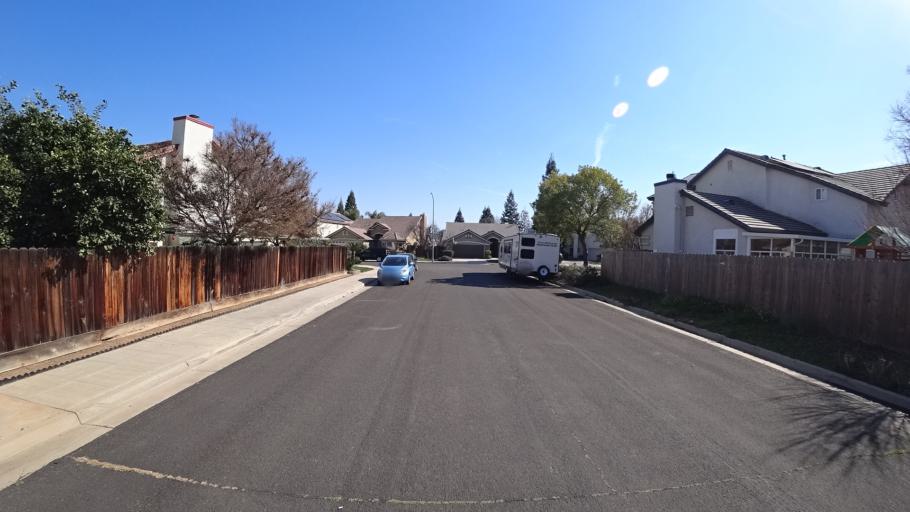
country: US
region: California
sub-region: Fresno County
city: Clovis
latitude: 36.8866
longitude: -119.7419
